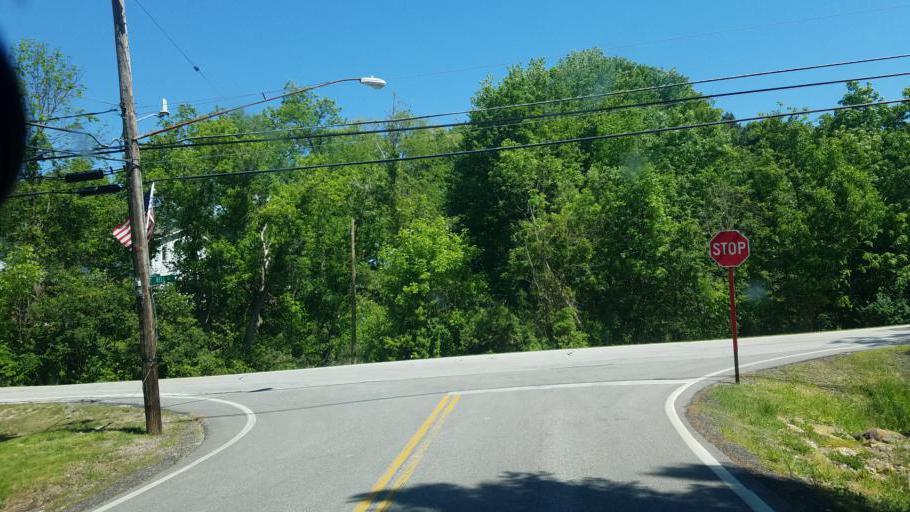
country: US
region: Ohio
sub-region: Geauga County
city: Bainbridge
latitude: 41.4317
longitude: -81.3086
